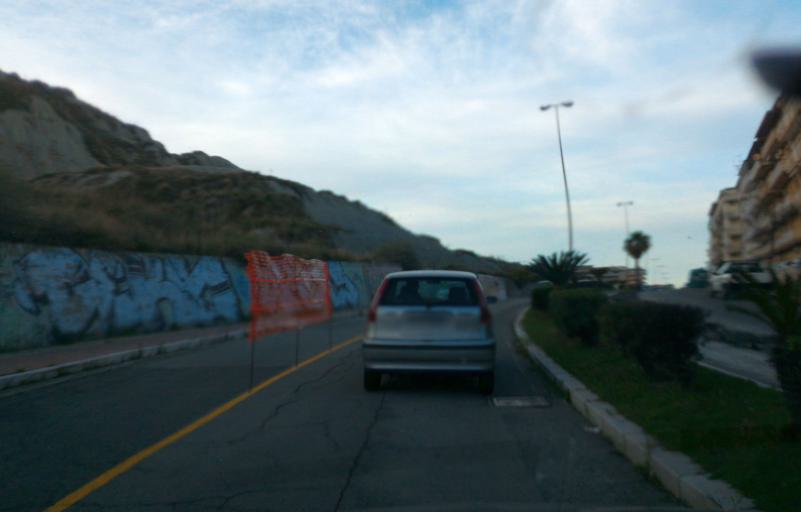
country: IT
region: Calabria
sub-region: Provincia di Crotone
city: Crotone
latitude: 39.0675
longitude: 17.1291
